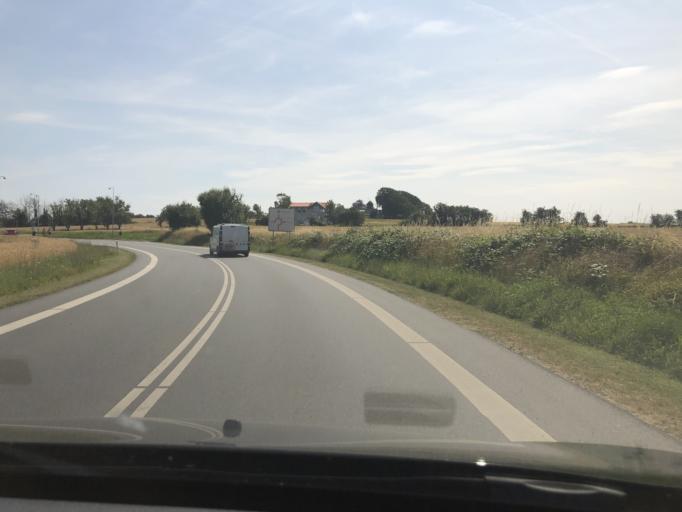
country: DK
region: South Denmark
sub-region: AEro Kommune
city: AEroskobing
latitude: 54.8866
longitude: 10.4056
